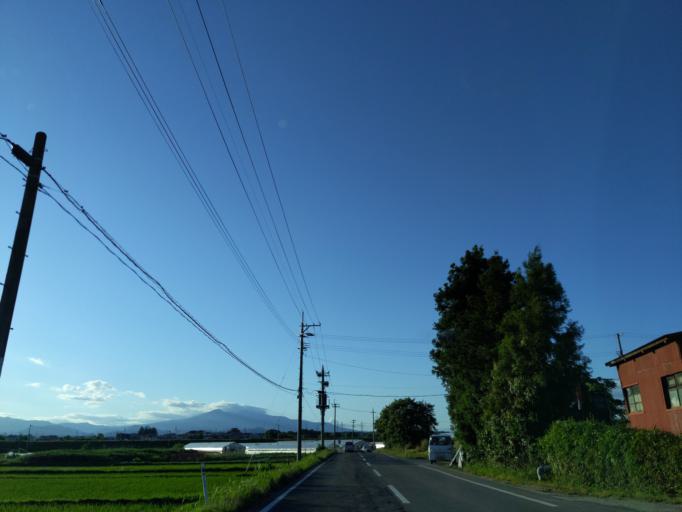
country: JP
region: Fukushima
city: Koriyama
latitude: 37.4105
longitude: 140.4126
